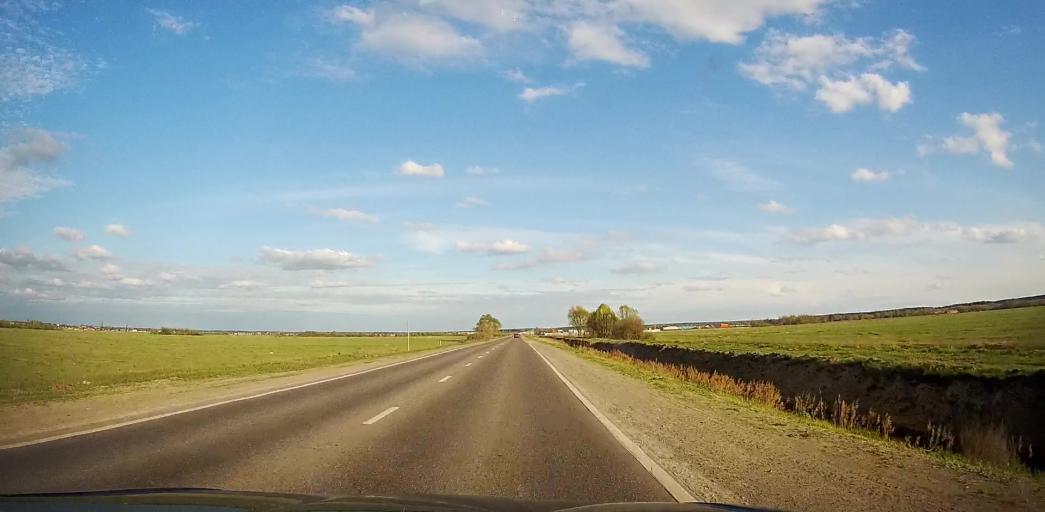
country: RU
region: Moskovskaya
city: Malyshevo
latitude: 55.5020
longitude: 38.2975
